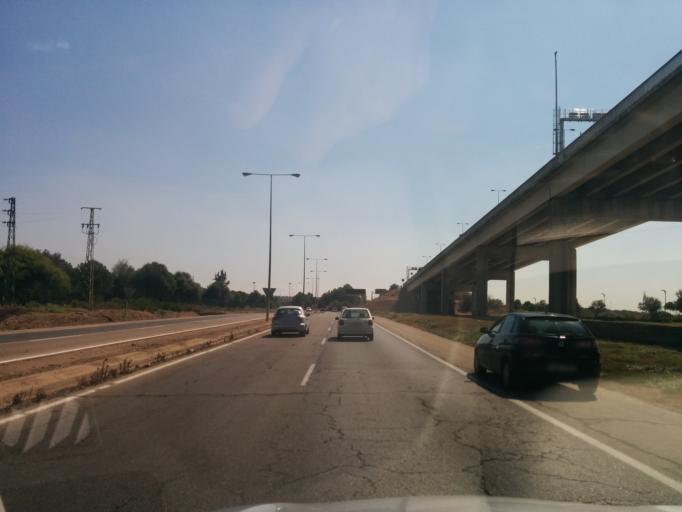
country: ES
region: Andalusia
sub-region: Provincia de Sevilla
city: Gelves
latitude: 37.3457
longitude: -5.9886
